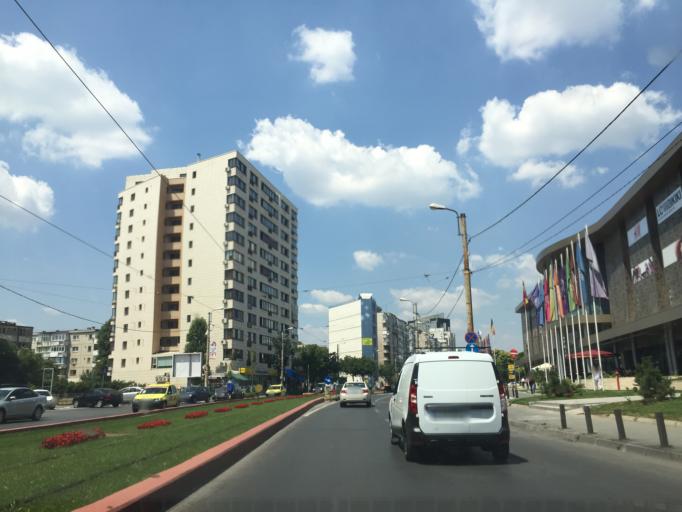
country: RO
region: Bucuresti
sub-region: Municipiul Bucuresti
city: Bucharest
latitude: 44.4193
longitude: 26.1266
